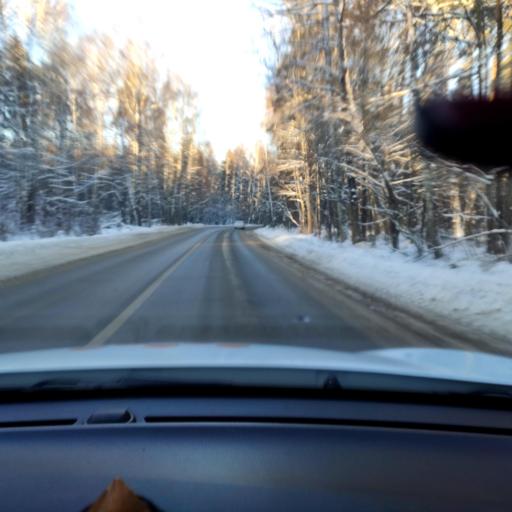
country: RU
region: Tatarstan
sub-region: Zelenodol'skiy Rayon
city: Vasil'yevo
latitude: 55.8827
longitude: 48.7221
